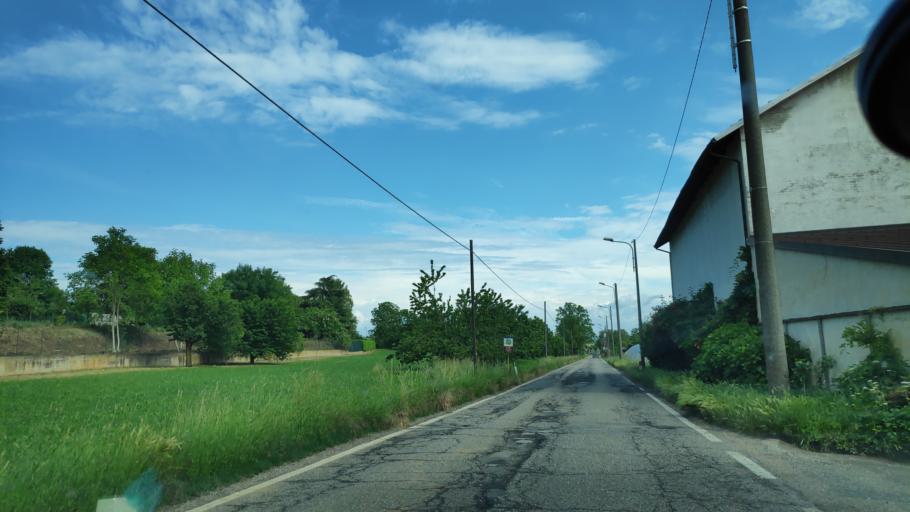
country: IT
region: Piedmont
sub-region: Provincia di Torino
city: Pecetto
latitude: 45.0004
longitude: 7.7687
